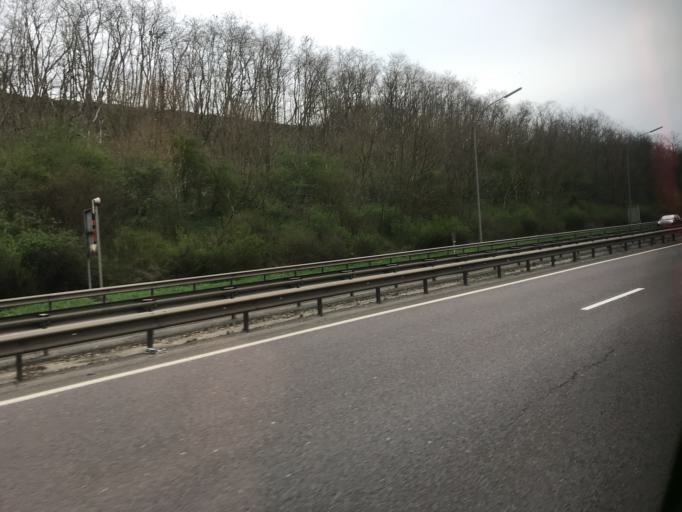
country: LU
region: Luxembourg
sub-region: Canton d'Esch-sur-Alzette
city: Leudelange
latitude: 49.5805
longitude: 6.0876
